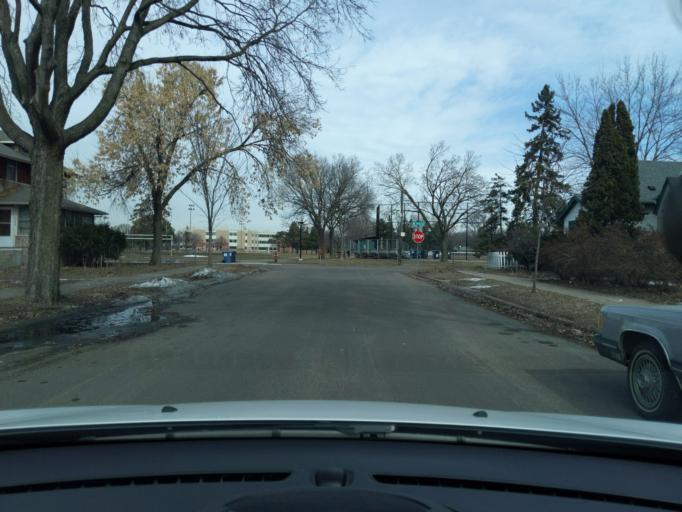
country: US
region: Minnesota
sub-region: Hennepin County
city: Saint Anthony
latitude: 45.0013
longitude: -93.2397
